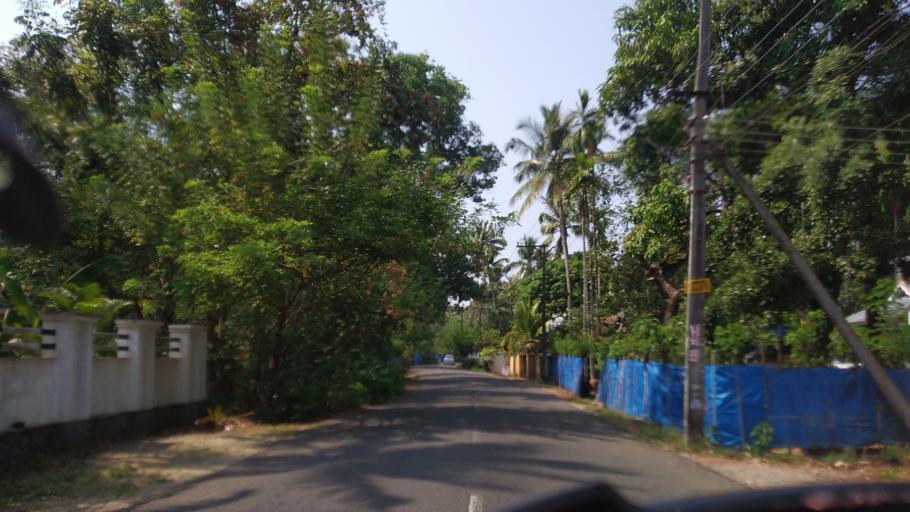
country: IN
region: Kerala
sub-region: Thrissur District
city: Thanniyam
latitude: 10.3286
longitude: 76.1219
